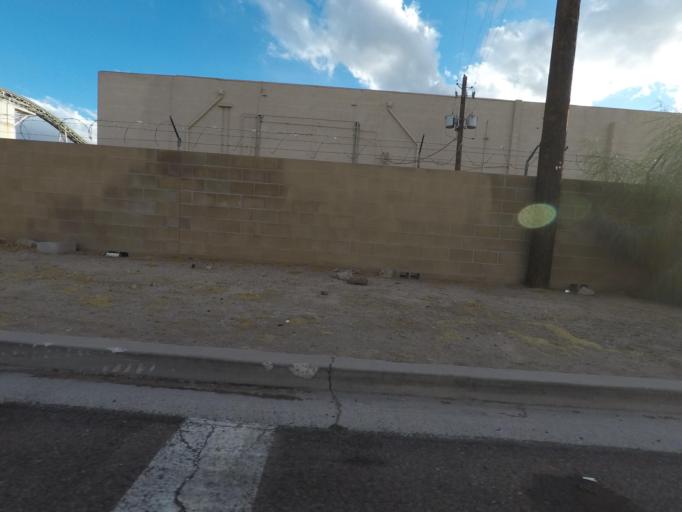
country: US
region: Arizona
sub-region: Maricopa County
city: Glendale
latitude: 33.5052
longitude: -112.1506
